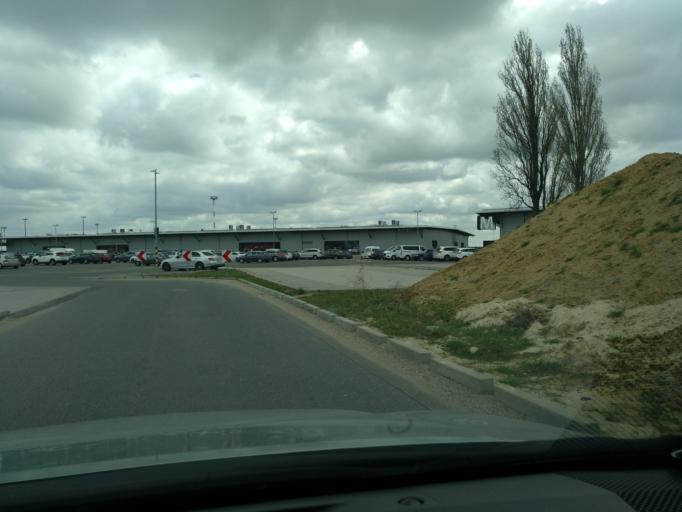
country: DE
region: Brandenburg
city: Schonefeld
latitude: 52.3888
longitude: 13.5143
